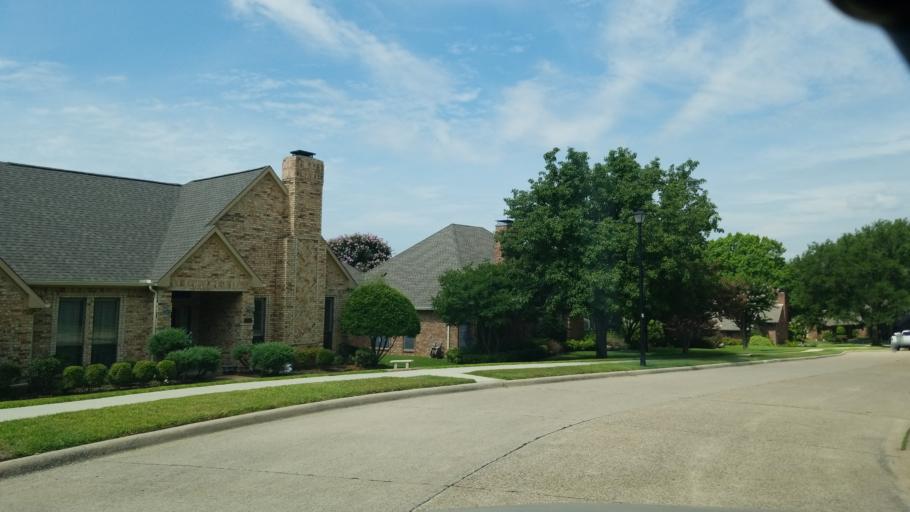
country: US
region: Texas
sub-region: Dallas County
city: Coppell
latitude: 32.9600
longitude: -96.9719
